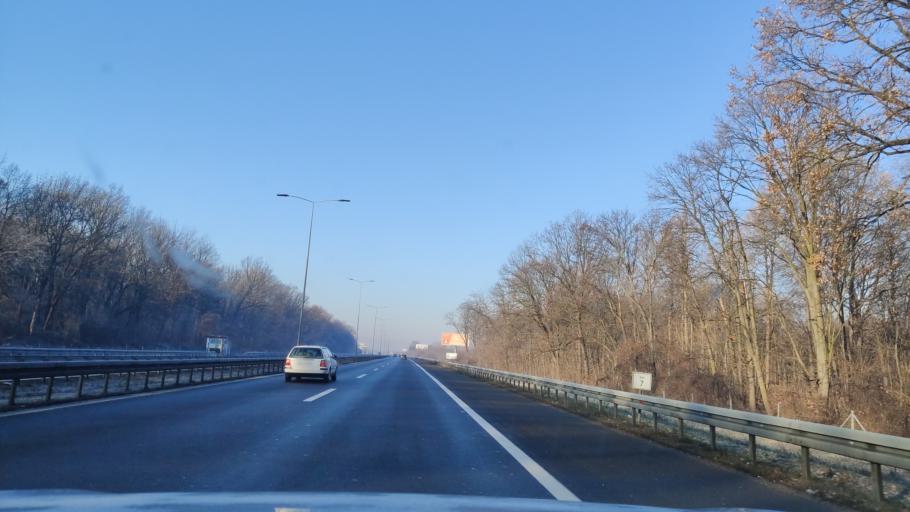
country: RS
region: Central Serbia
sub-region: Belgrade
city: Zemun
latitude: 44.8344
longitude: 20.3391
